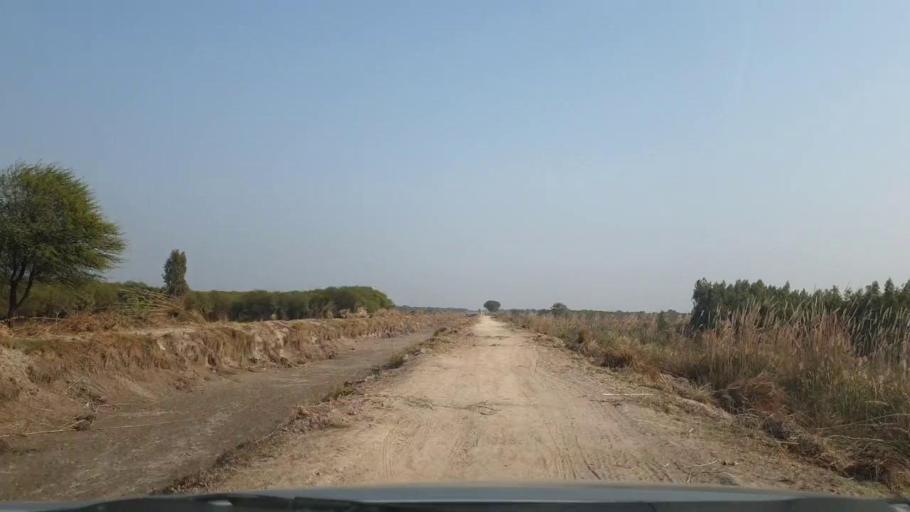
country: PK
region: Sindh
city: Tando Adam
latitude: 25.6464
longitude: 68.5995
